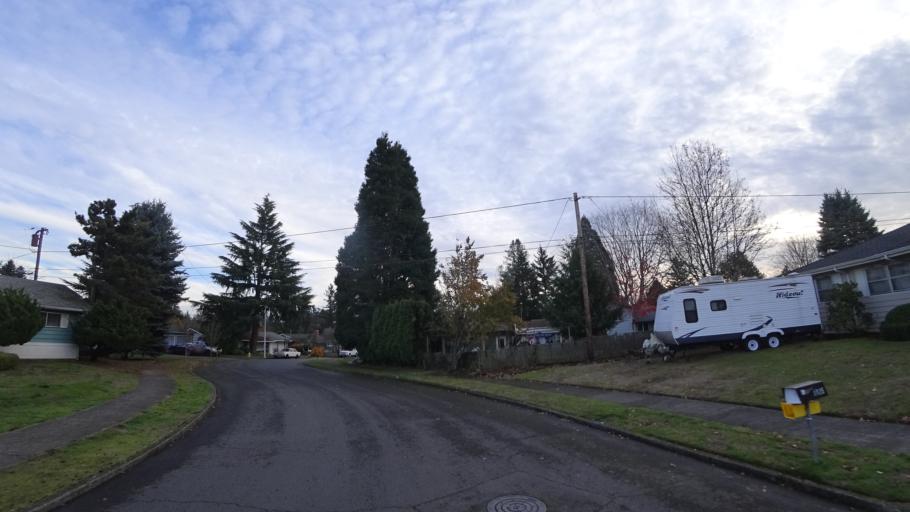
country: US
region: Oregon
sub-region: Multnomah County
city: Lents
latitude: 45.5159
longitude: -122.5162
